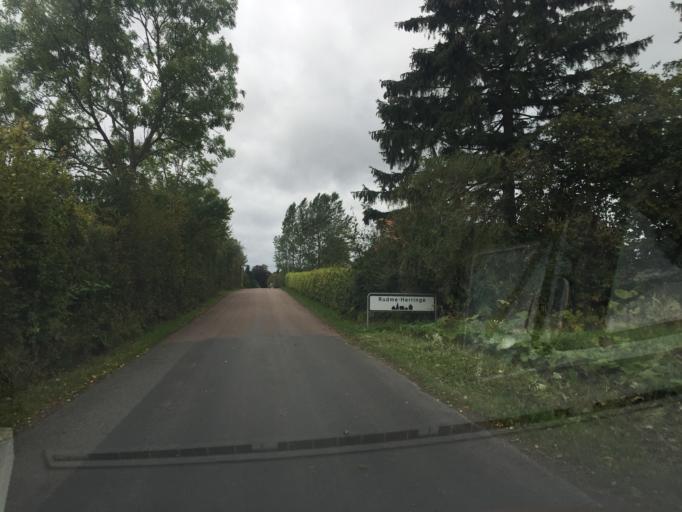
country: DK
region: South Denmark
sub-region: Faaborg-Midtfyn Kommune
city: Ringe
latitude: 55.1996
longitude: 10.4694
